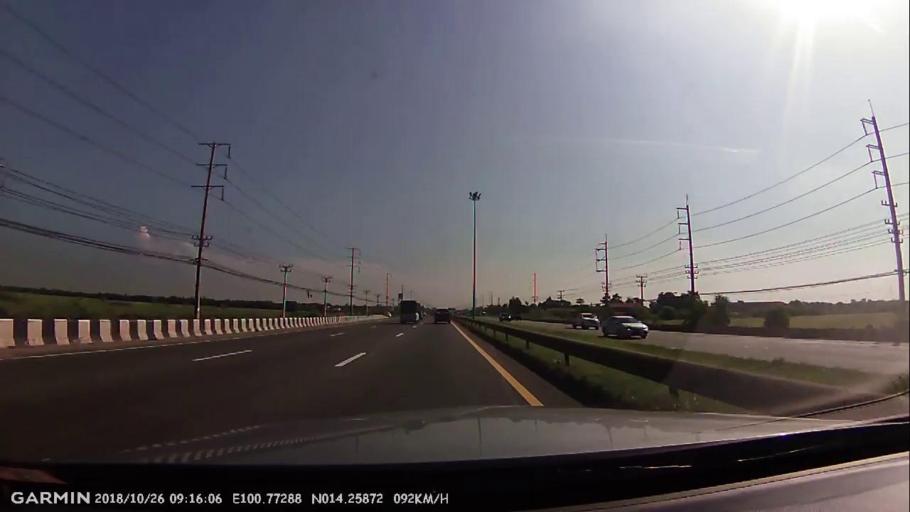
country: TH
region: Phra Nakhon Si Ayutthaya
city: Wang Noi
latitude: 14.2587
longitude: 100.7726
